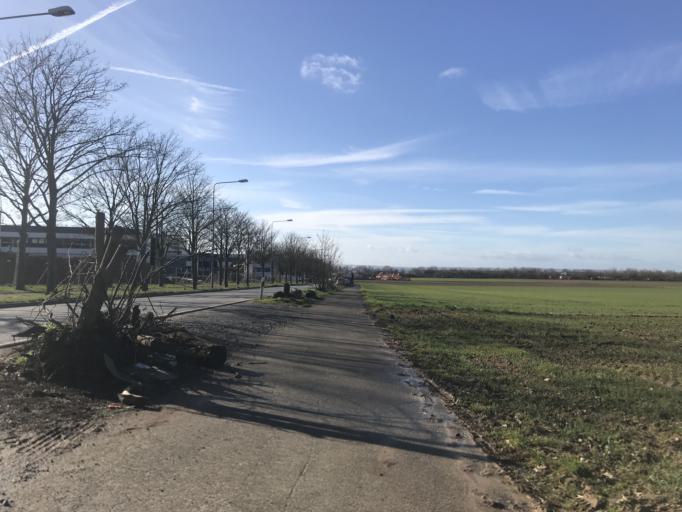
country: DE
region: Hesse
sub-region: Regierungsbezirk Darmstadt
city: Hochheim am Main
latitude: 50.0606
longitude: 8.3290
